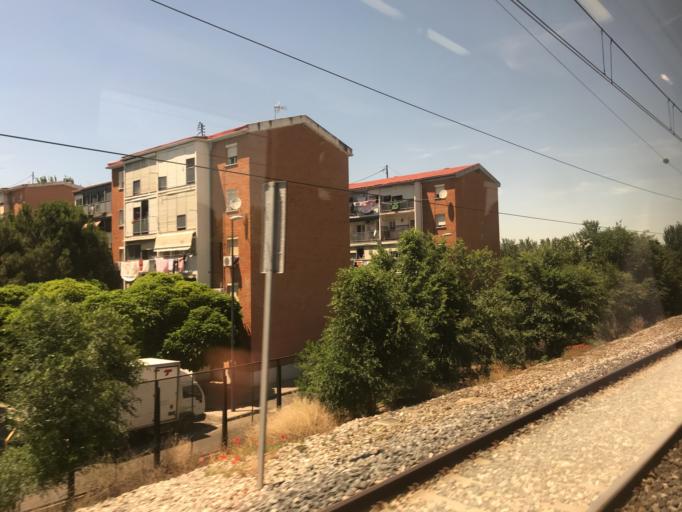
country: ES
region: Madrid
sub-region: Provincia de Madrid
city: Villaverde
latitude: 40.3434
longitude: -3.6839
